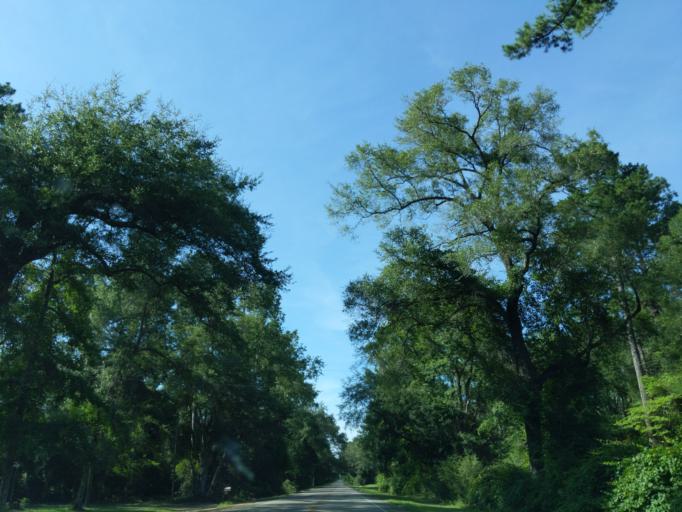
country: US
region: Florida
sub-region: Leon County
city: Woodville
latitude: 30.2528
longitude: -84.3130
